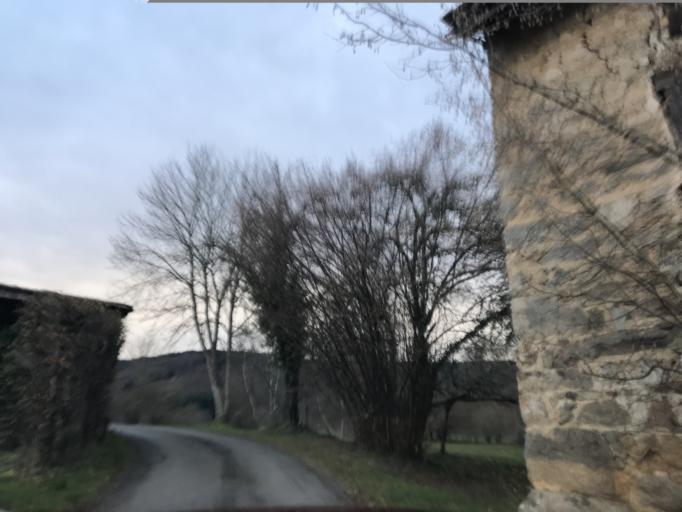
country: FR
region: Auvergne
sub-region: Departement du Puy-de-Dome
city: Celles-sur-Durolle
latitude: 45.8351
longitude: 3.6658
